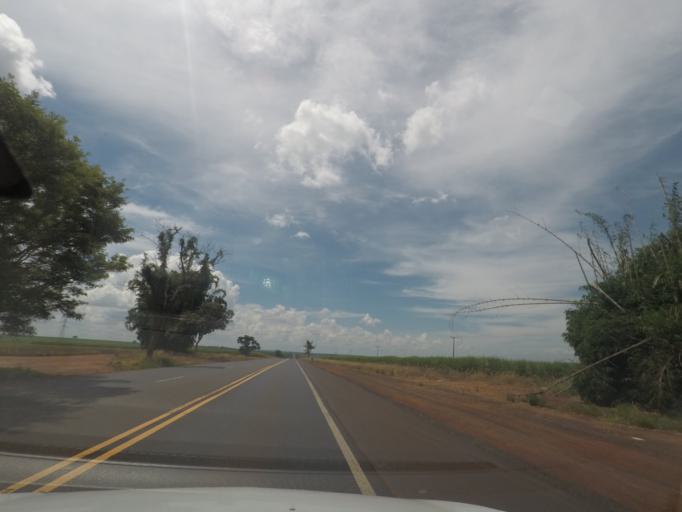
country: BR
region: Sao Paulo
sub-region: Barretos
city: Barretos
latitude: -20.2749
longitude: -48.6723
